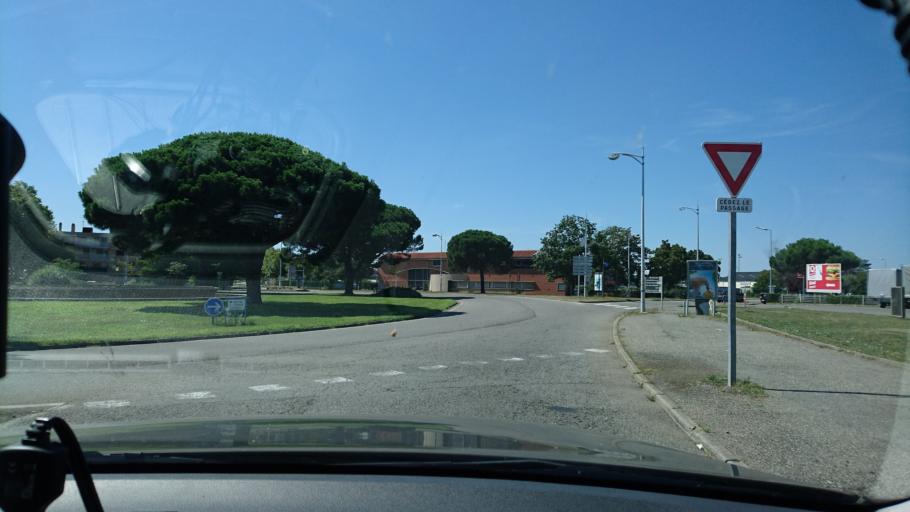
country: FR
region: Midi-Pyrenees
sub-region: Departement de la Haute-Garonne
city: Colomiers
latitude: 43.6095
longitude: 1.3528
